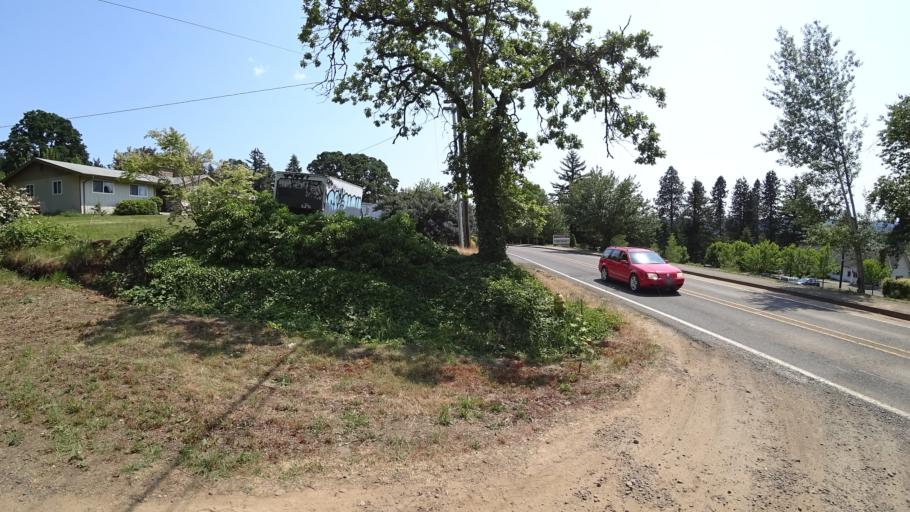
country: US
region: Oregon
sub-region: Multnomah County
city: Lents
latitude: 45.4482
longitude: -122.5676
